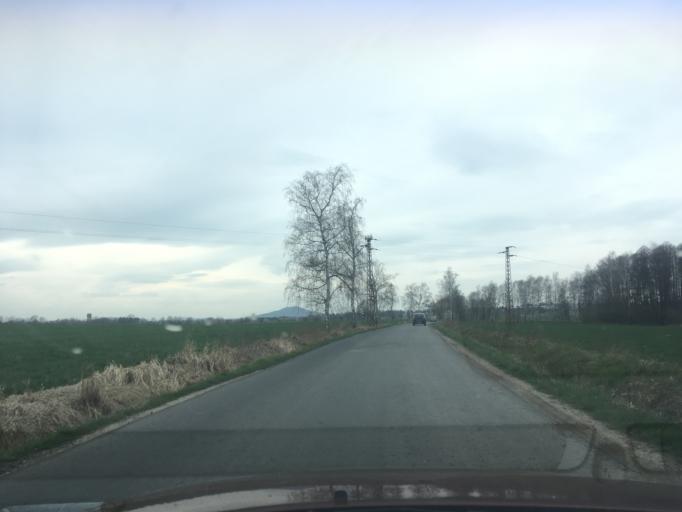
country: PL
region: Lower Silesian Voivodeship
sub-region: Powiat zgorzelecki
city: Lagow
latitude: 51.1421
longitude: 15.0470
